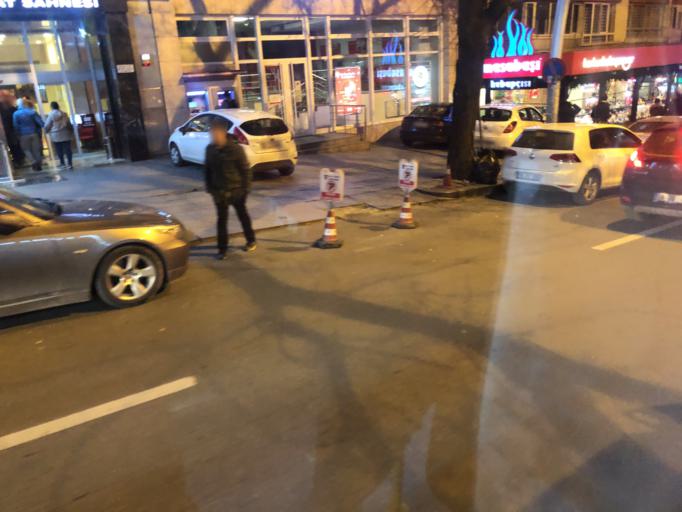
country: TR
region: Ankara
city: Cankaya
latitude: 39.9189
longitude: 32.8596
